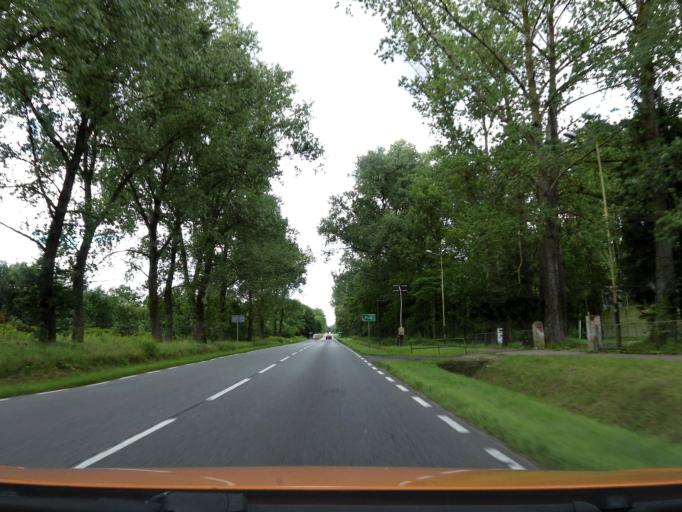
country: PL
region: West Pomeranian Voivodeship
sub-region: Powiat gryficki
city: Ploty
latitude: 53.8107
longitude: 15.2752
